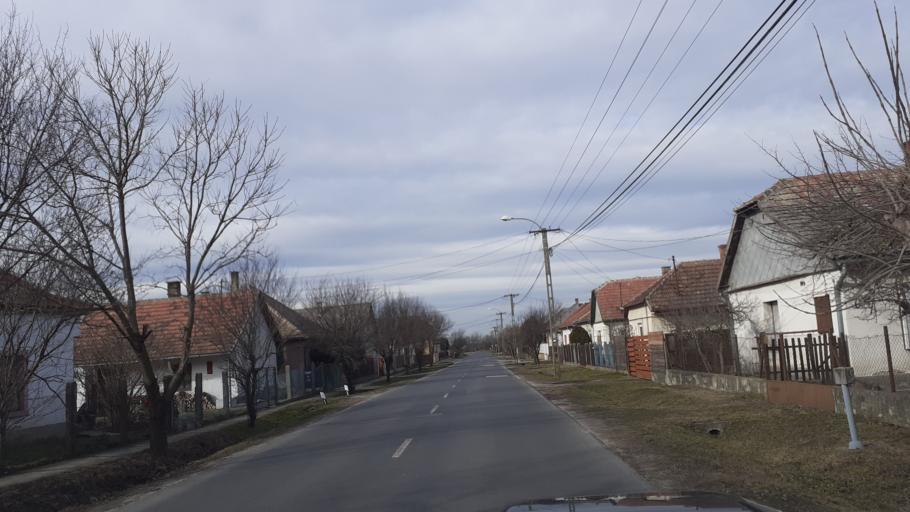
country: HU
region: Fejer
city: Sarbogard
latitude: 46.9057
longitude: 18.5973
